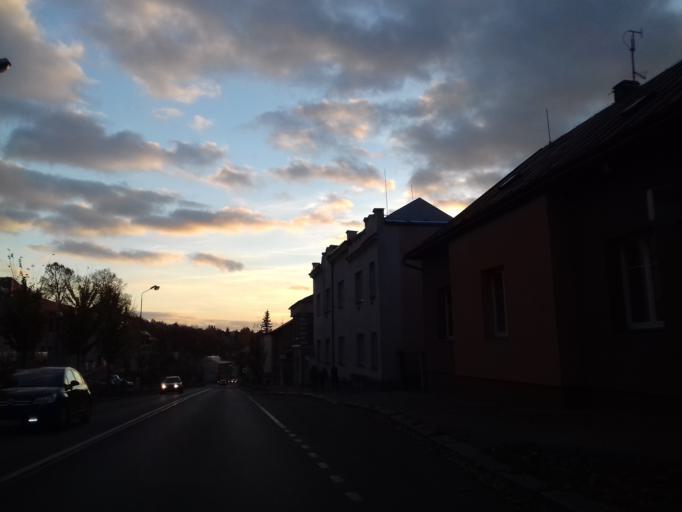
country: CZ
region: Pardubicky
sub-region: Okres Chrudim
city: Hlinsko
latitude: 49.7634
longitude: 15.9121
